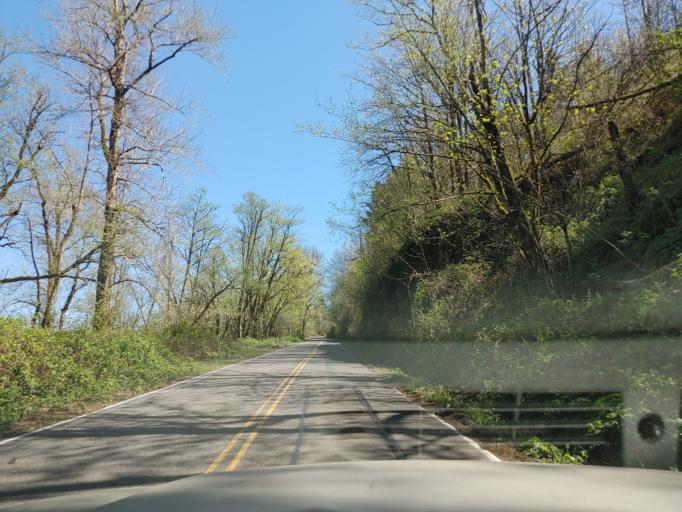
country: US
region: Washington
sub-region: Clark County
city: Washougal
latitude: 45.5397
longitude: -122.2875
